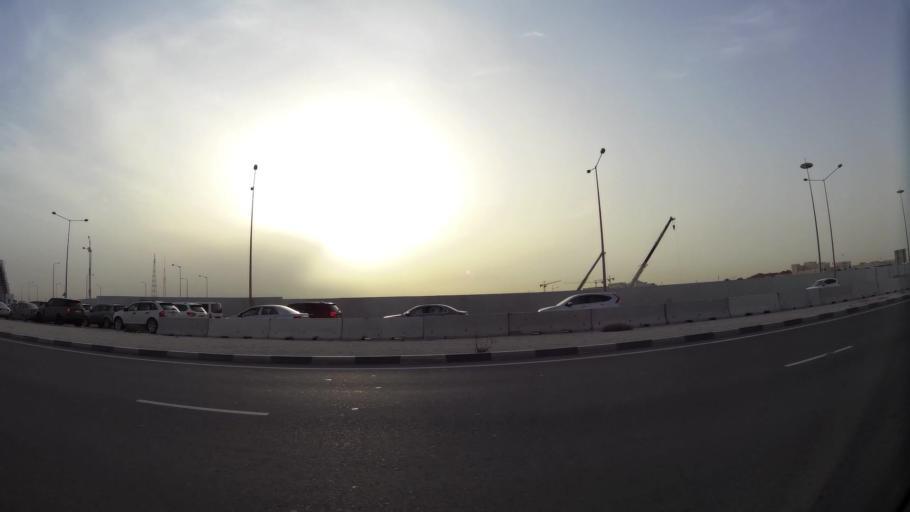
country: QA
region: Baladiyat ad Dawhah
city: Doha
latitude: 25.3407
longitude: 51.5213
